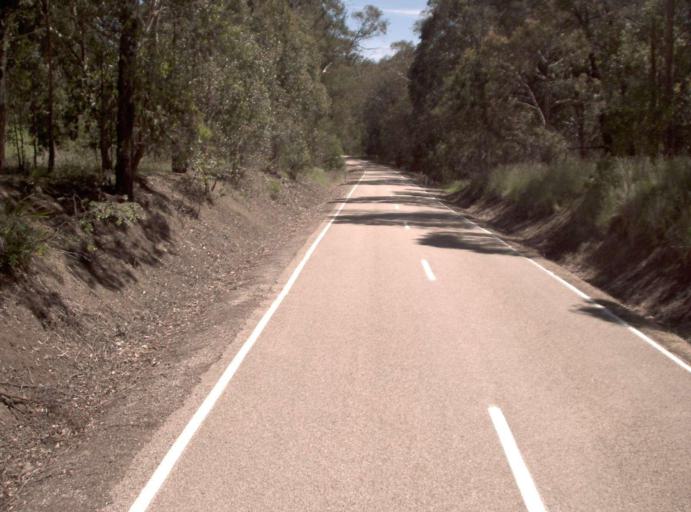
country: AU
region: Victoria
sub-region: East Gippsland
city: Lakes Entrance
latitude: -37.2718
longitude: 148.2559
